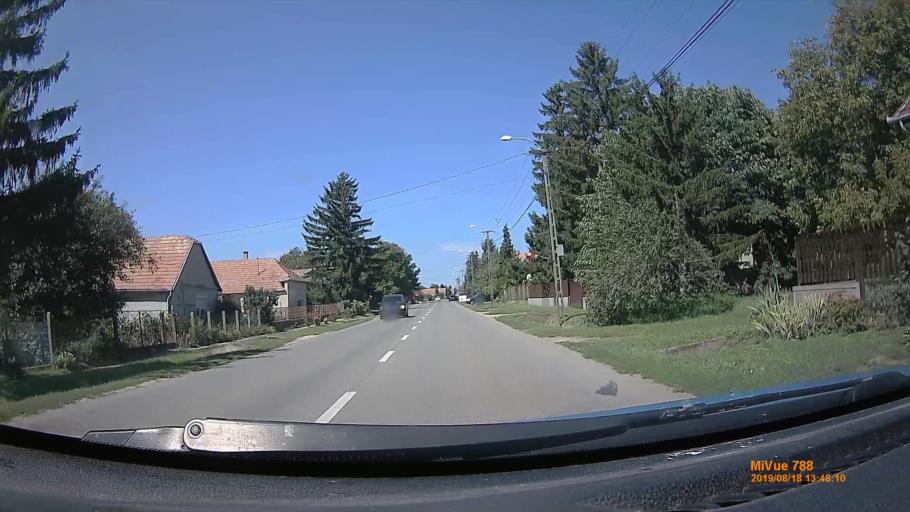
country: HU
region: Fejer
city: Cece
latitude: 46.7585
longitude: 18.6377
